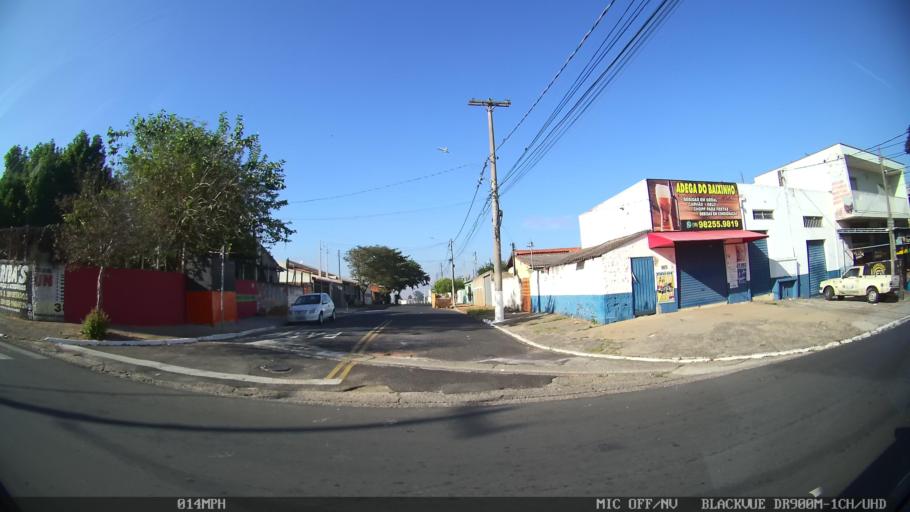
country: BR
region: Sao Paulo
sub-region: Hortolandia
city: Hortolandia
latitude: -22.8962
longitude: -47.1650
